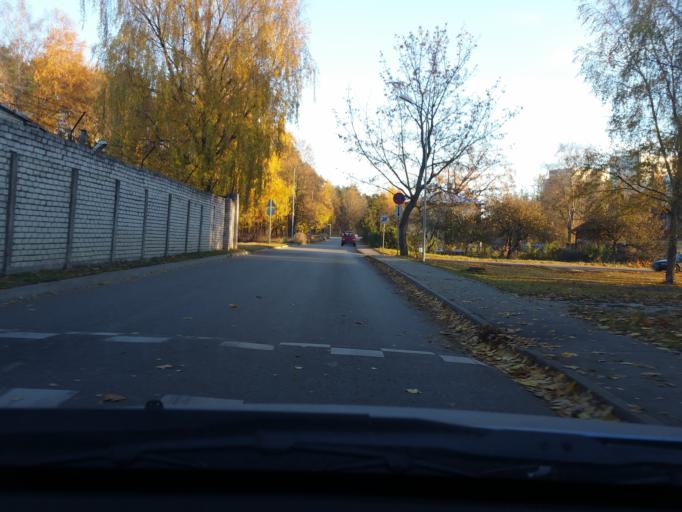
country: LV
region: Riga
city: Jaunciems
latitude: 56.9635
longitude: 24.1974
